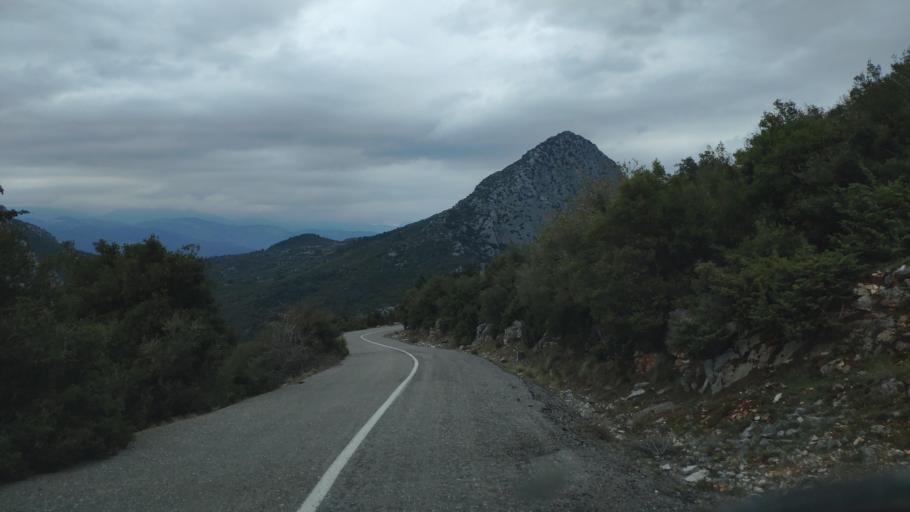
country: GR
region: Central Greece
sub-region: Nomos Fokidos
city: Amfissa
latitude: 38.6437
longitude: 22.4200
